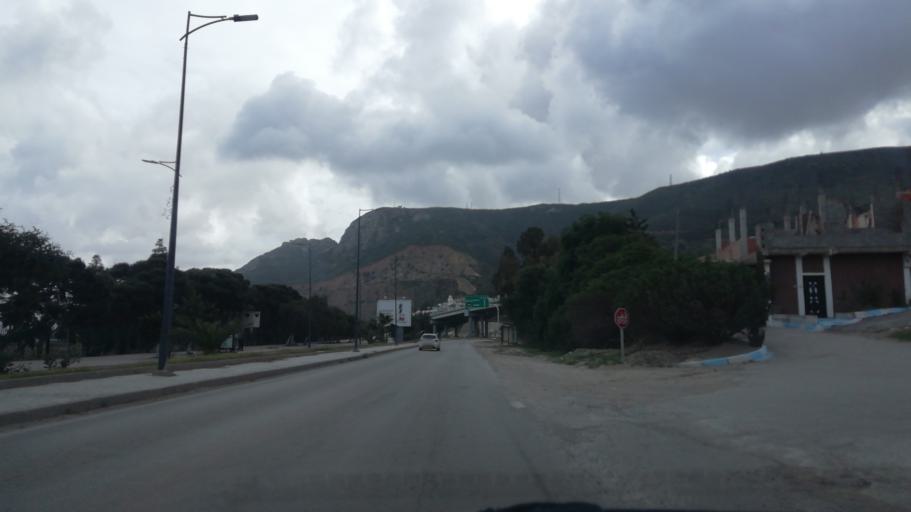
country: DZ
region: Oran
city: Mers el Kebir
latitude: 35.7161
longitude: -0.6941
